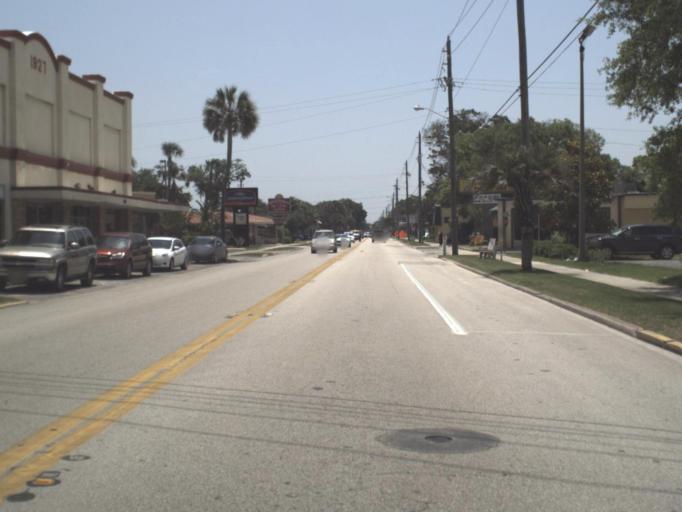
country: US
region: Florida
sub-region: Saint Johns County
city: Saint Augustine
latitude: 29.9068
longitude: -81.3189
